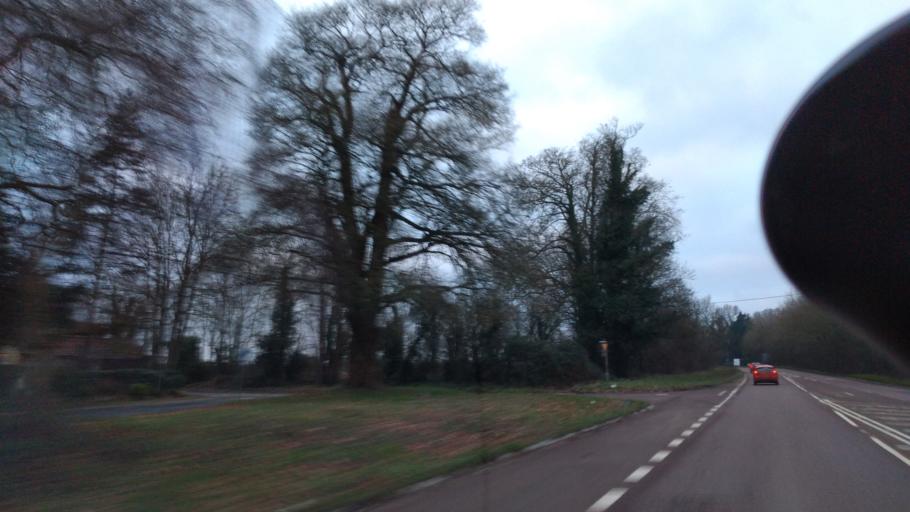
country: GB
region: England
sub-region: Wiltshire
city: Lacock
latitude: 51.4288
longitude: -2.1295
